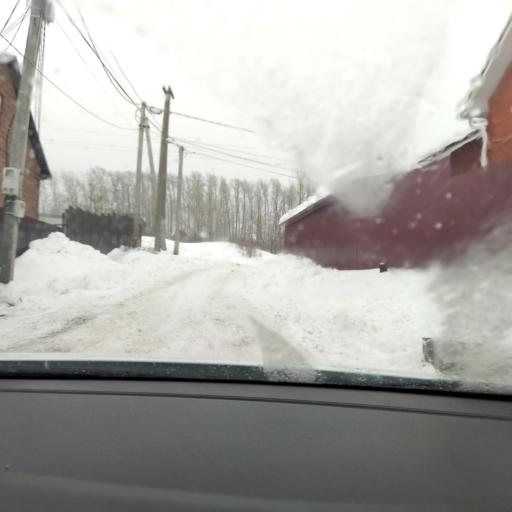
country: RU
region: Bashkortostan
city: Ufa
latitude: 54.6080
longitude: 55.9478
